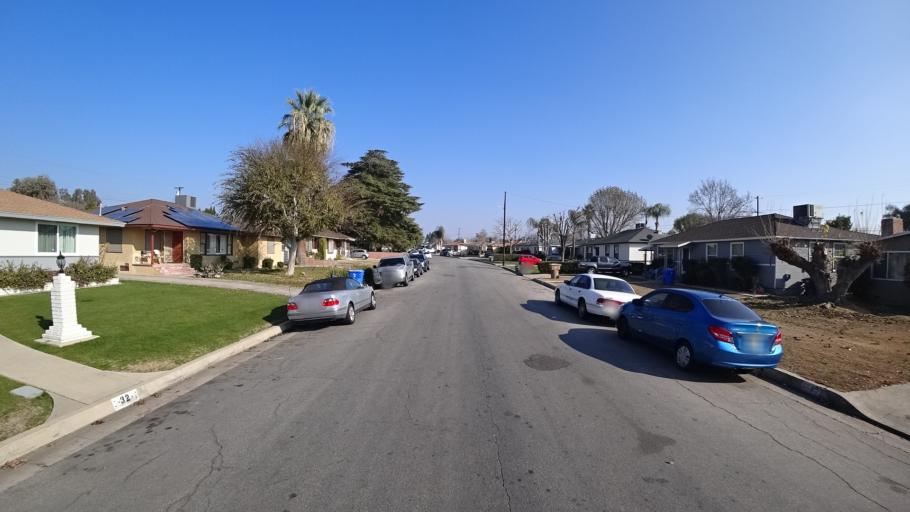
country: US
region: California
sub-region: Kern County
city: Bakersfield
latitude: 35.3921
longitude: -119.0011
